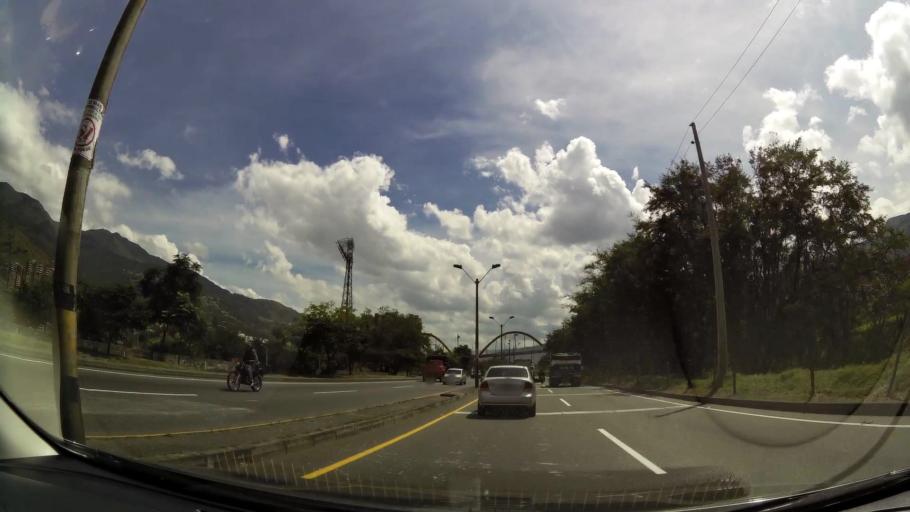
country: CO
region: Antioquia
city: Bello
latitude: 6.3332
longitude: -75.5464
